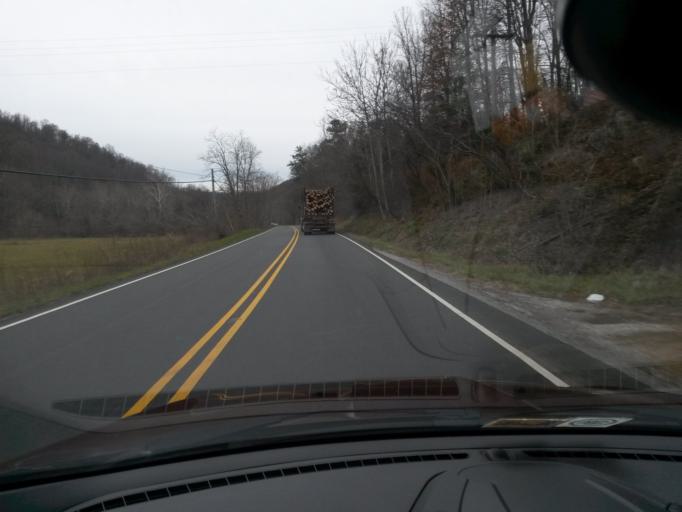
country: US
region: Virginia
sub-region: City of Buena Vista
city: Buena Vista
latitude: 37.6768
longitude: -79.2192
